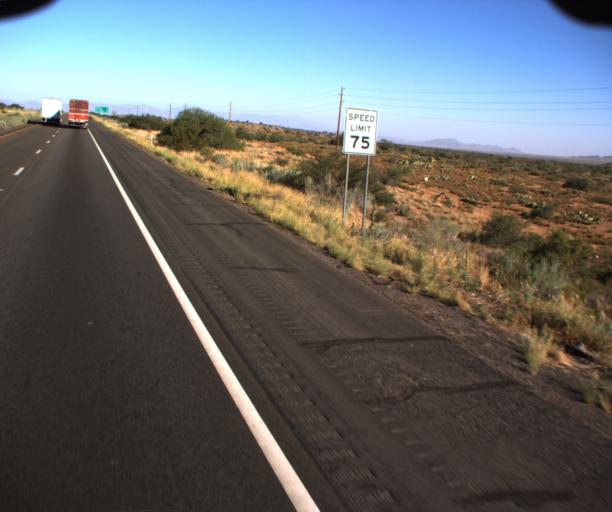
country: US
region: Arizona
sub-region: Mohave County
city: New Kingman-Butler
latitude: 35.1822
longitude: -113.8019
